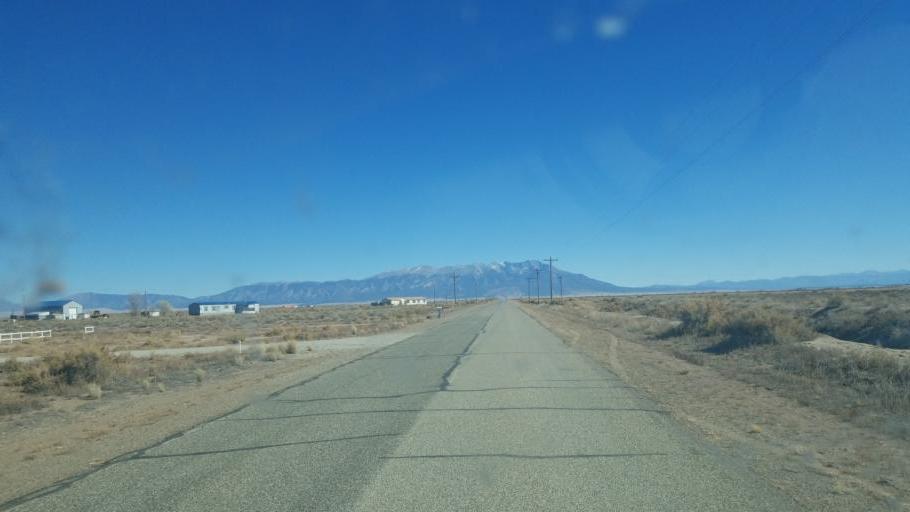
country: US
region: Colorado
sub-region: Alamosa County
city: Alamosa
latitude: 37.5746
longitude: -105.9041
